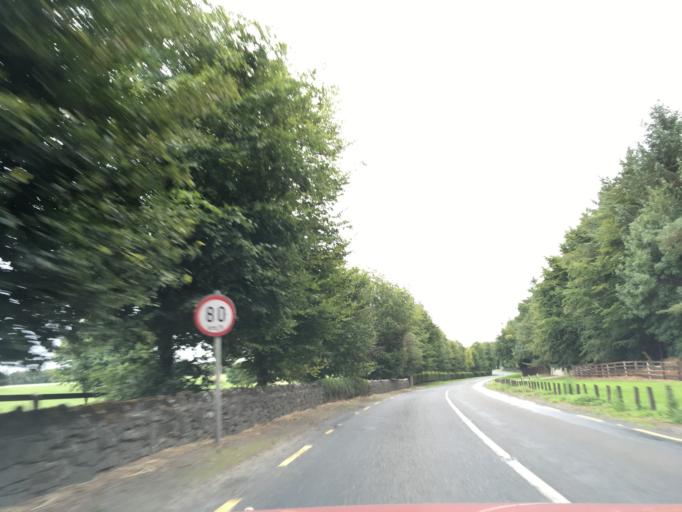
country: IE
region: Munster
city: Cashel
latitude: 52.4643
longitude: -7.8289
